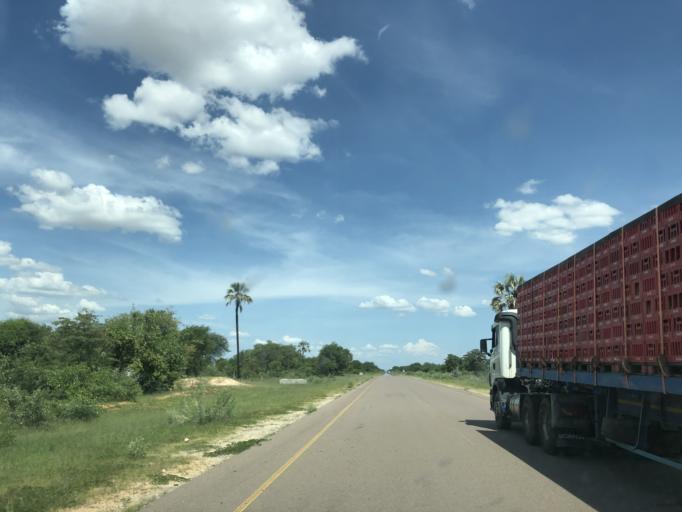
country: AO
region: Cunene
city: Ondjiva
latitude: -16.8954
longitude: 15.5027
